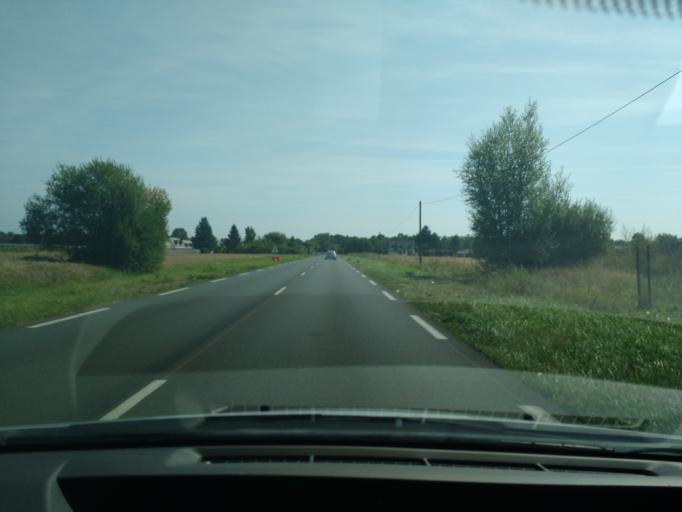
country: FR
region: Pays de la Loire
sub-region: Departement de Maine-et-Loire
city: Andard
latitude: 47.4650
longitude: -0.4033
